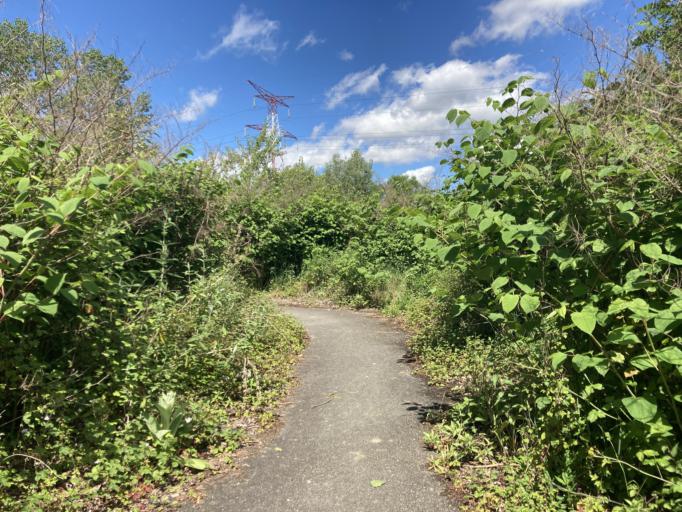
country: FR
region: Aquitaine
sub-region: Departement des Pyrenees-Atlantiques
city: Arbus
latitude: 43.3387
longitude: -0.4976
